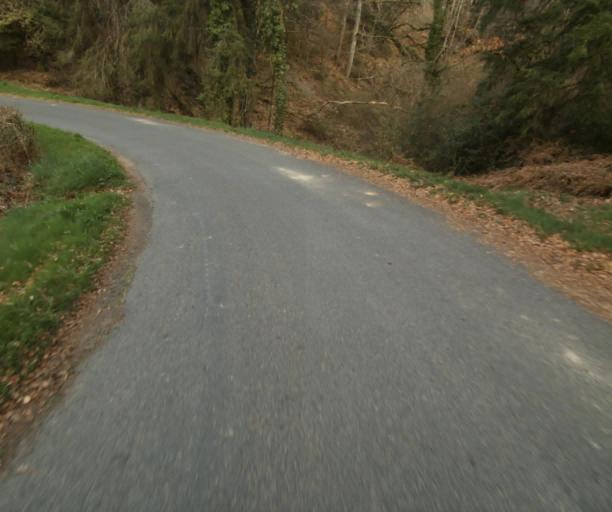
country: FR
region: Limousin
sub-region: Departement de la Correze
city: Chamboulive
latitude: 45.4460
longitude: 1.7721
